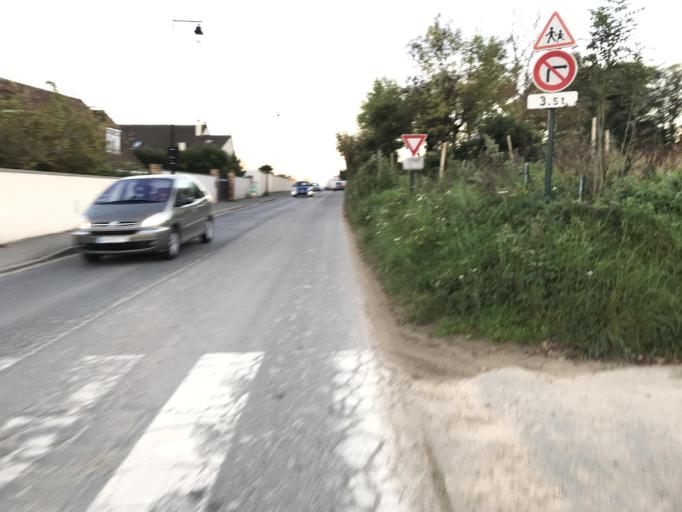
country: FR
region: Ile-de-France
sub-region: Departement de l'Essonne
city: Saulx-les-Chartreux
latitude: 48.6742
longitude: 2.2775
